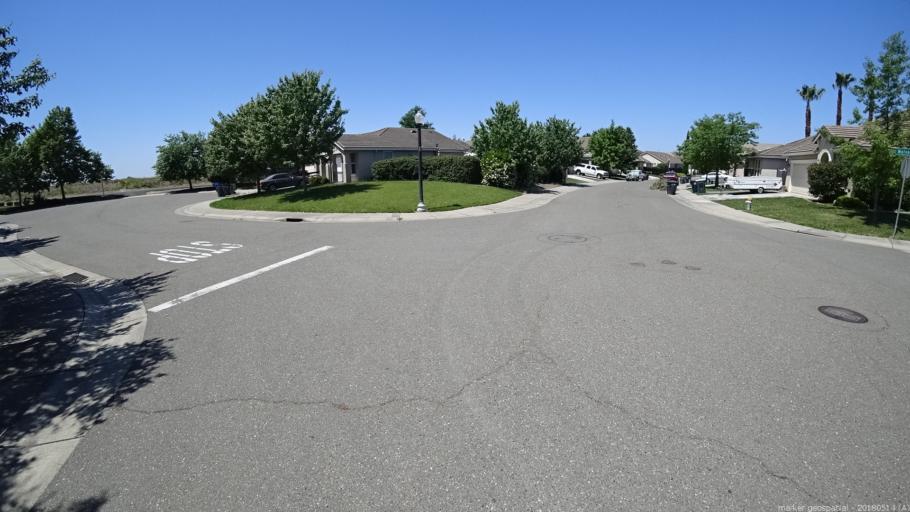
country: US
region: California
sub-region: Yolo County
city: West Sacramento
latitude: 38.6248
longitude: -121.5266
